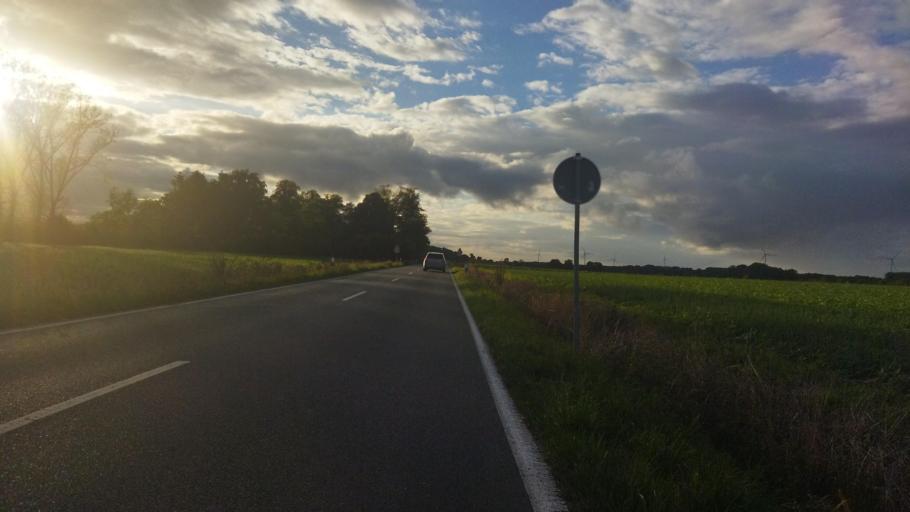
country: DE
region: North Rhine-Westphalia
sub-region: Regierungsbezirk Munster
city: Billerbeck
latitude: 51.9728
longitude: 7.2479
